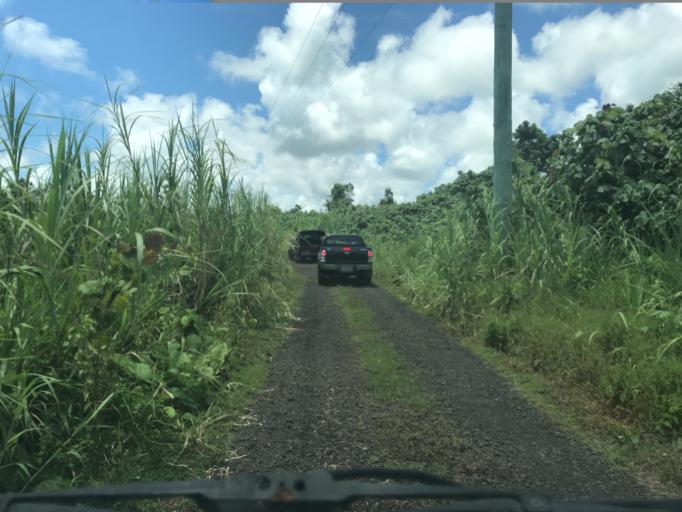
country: WS
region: Gagaifomauga
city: Safotu
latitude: -13.5583
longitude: -172.3003
